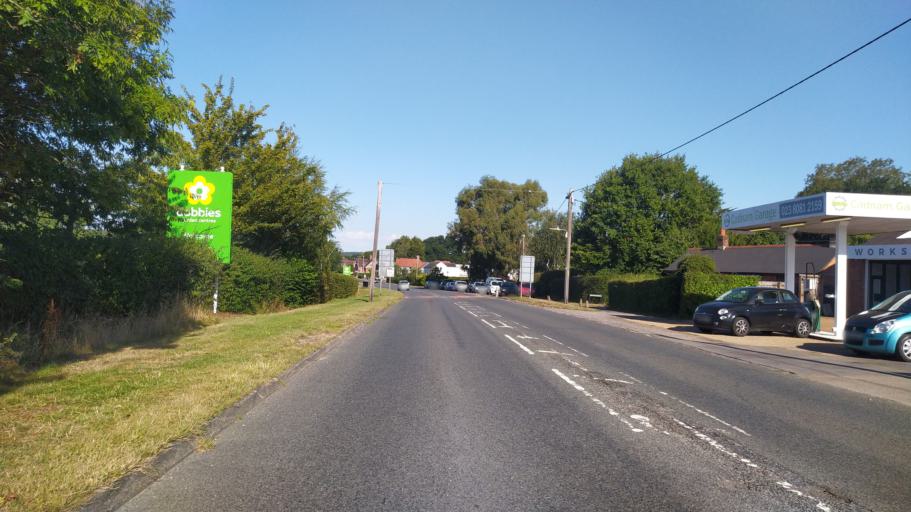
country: GB
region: England
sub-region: Hampshire
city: Cadnam
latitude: 50.9183
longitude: -1.5671
